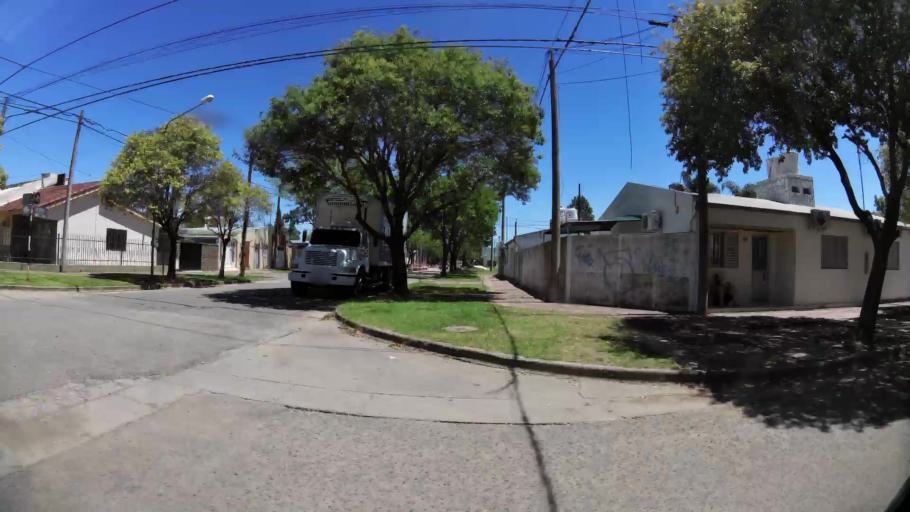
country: AR
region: Santa Fe
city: Rafaela
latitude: -31.2503
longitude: -61.4598
